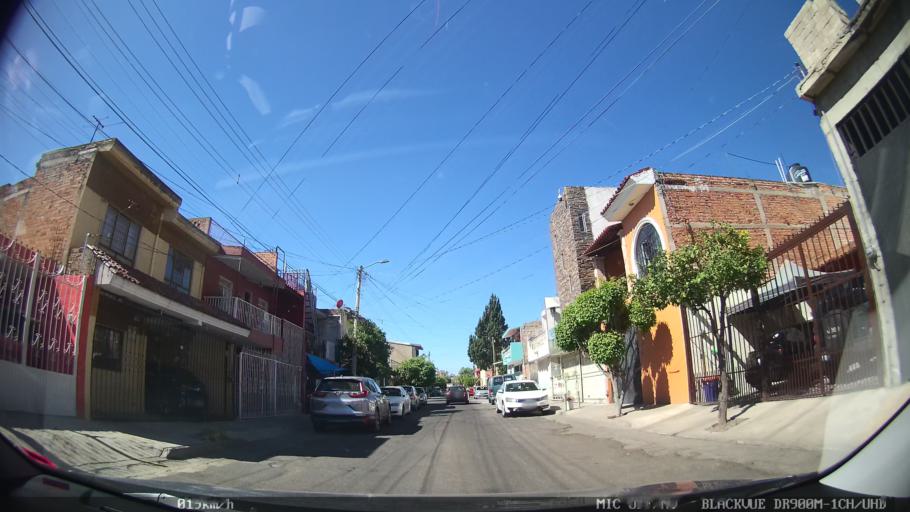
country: MX
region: Jalisco
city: Tlaquepaque
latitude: 20.6827
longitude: -103.2757
